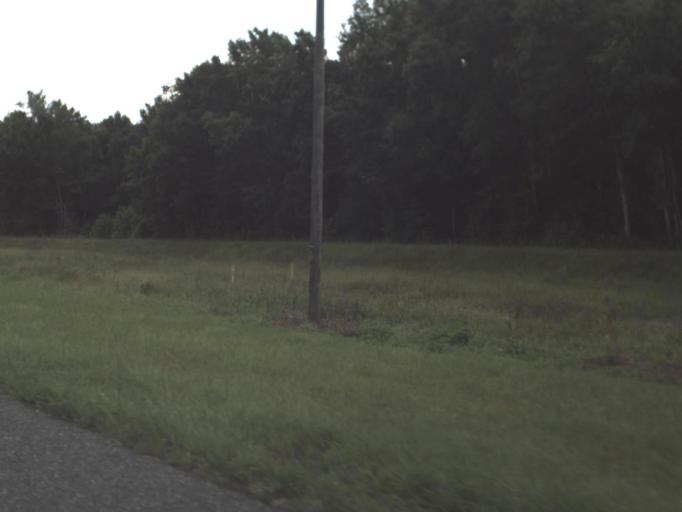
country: US
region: Florida
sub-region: Levy County
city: Inglis
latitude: 29.1774
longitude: -82.6638
